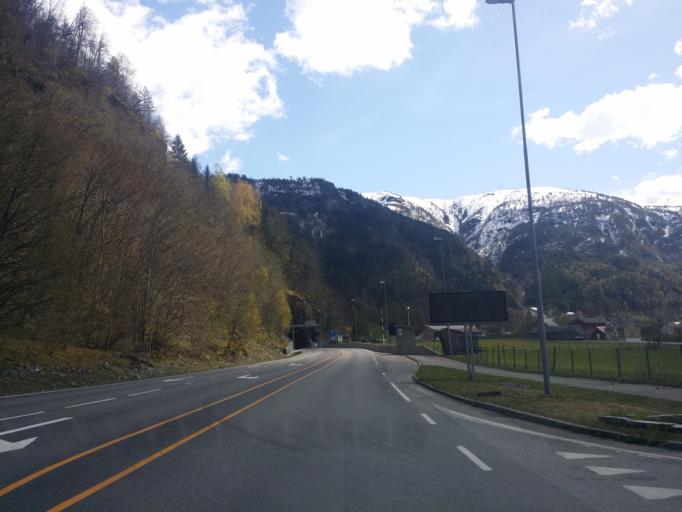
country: NO
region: Hordaland
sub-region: Granvin
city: Granvin
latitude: 60.5346
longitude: 6.7342
